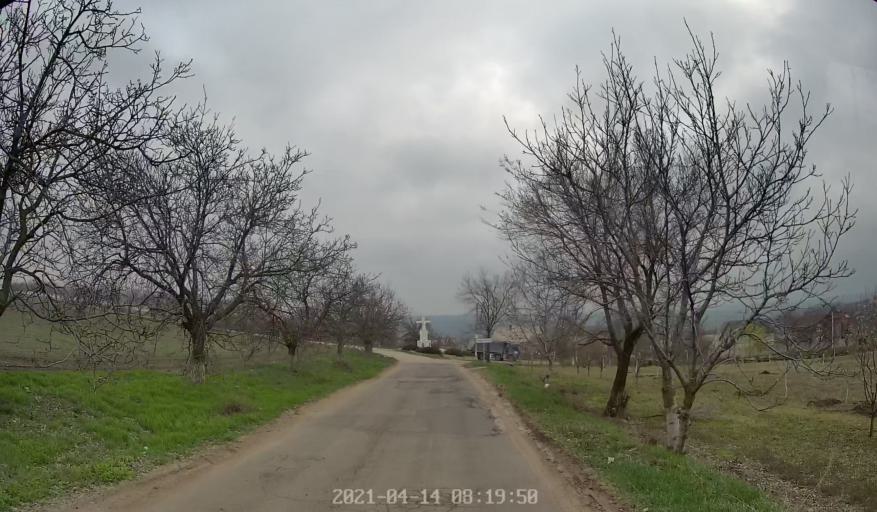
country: MD
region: Chisinau
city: Stauceni
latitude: 47.0637
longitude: 28.9193
